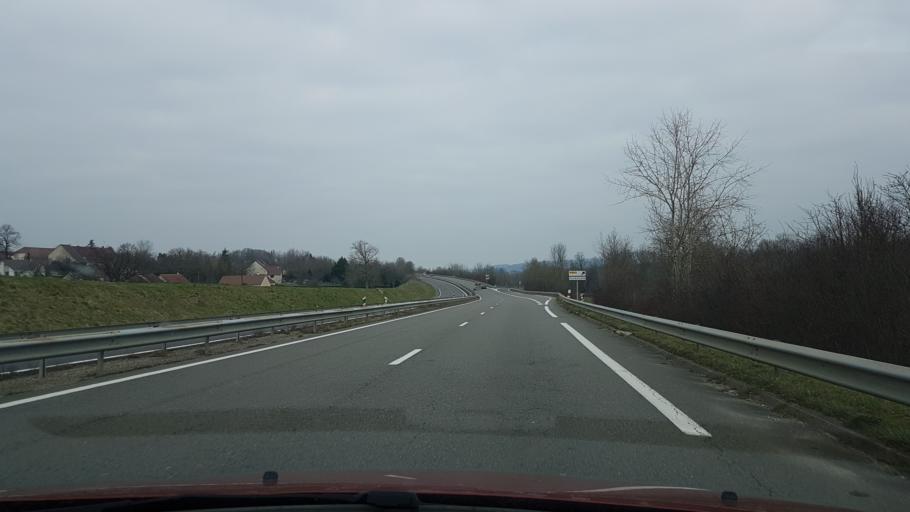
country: FR
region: Franche-Comte
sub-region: Departement du Jura
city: Lons-le-Saunier
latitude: 46.7298
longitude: 5.5583
